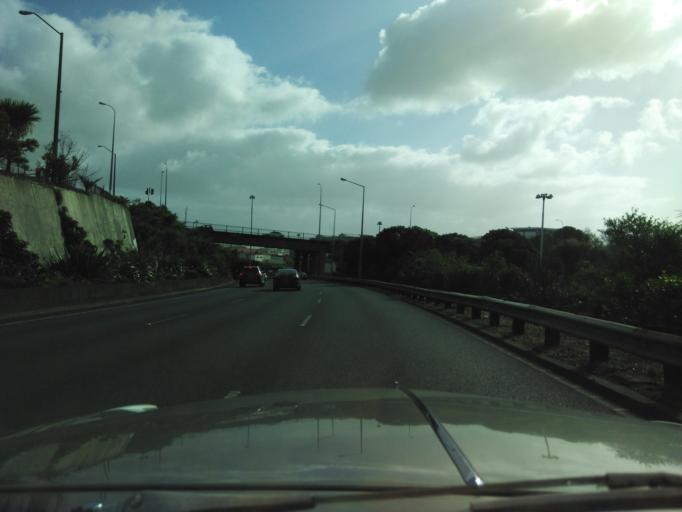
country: NZ
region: Auckland
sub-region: Auckland
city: Auckland
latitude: -36.8615
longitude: 174.7633
